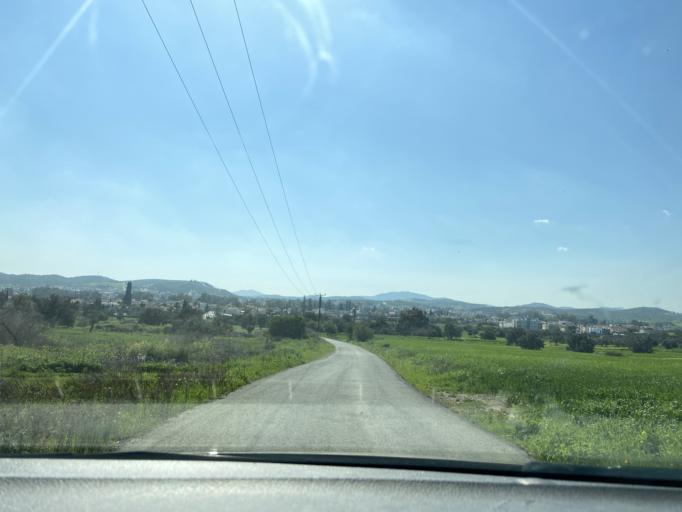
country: CY
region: Lefkosia
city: Dali
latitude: 35.0279
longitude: 33.3908
